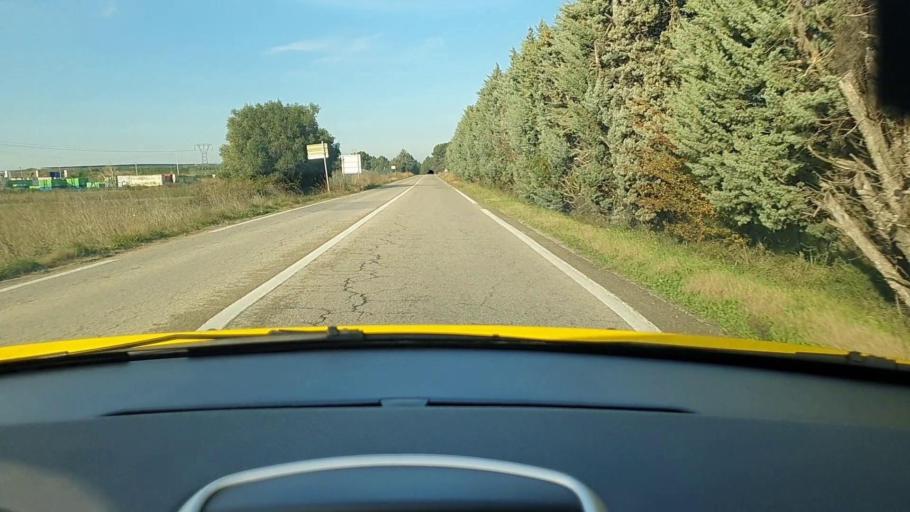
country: FR
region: Languedoc-Roussillon
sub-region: Departement du Gard
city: Comps
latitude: 43.8220
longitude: 4.5996
